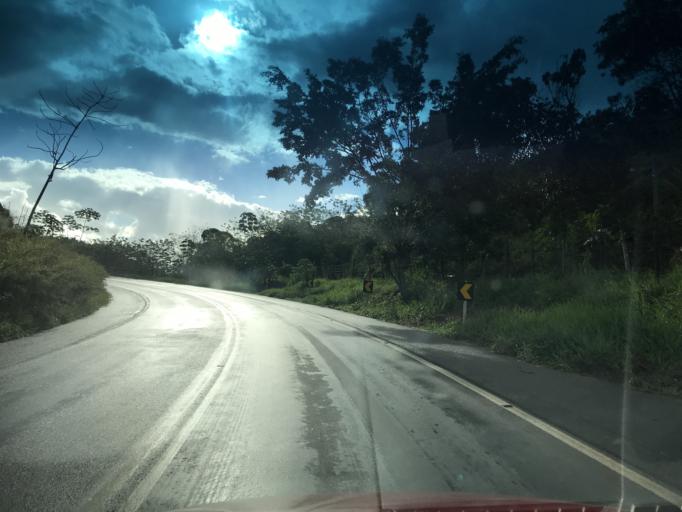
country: BR
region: Bahia
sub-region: Ibirapitanga
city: Ibirapitanga
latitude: -14.0117
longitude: -39.4362
